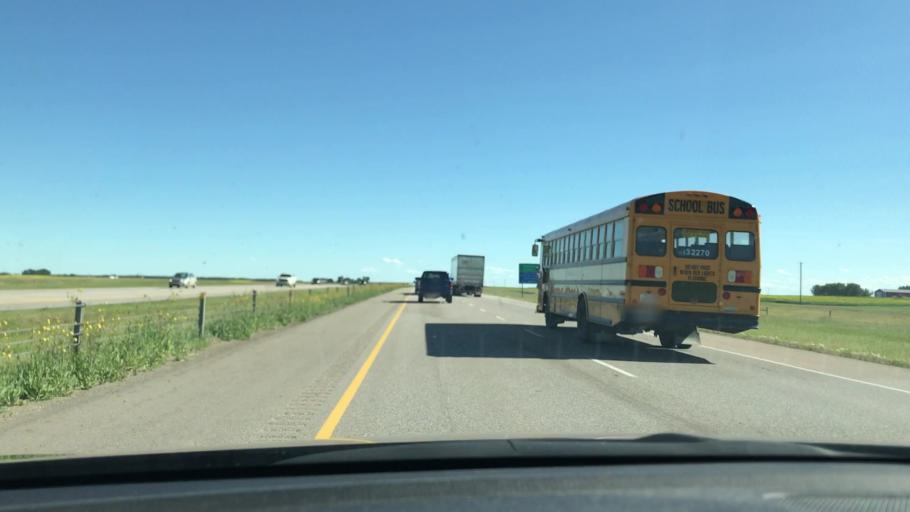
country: CA
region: Alberta
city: Didsbury
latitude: 51.6876
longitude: -114.0255
